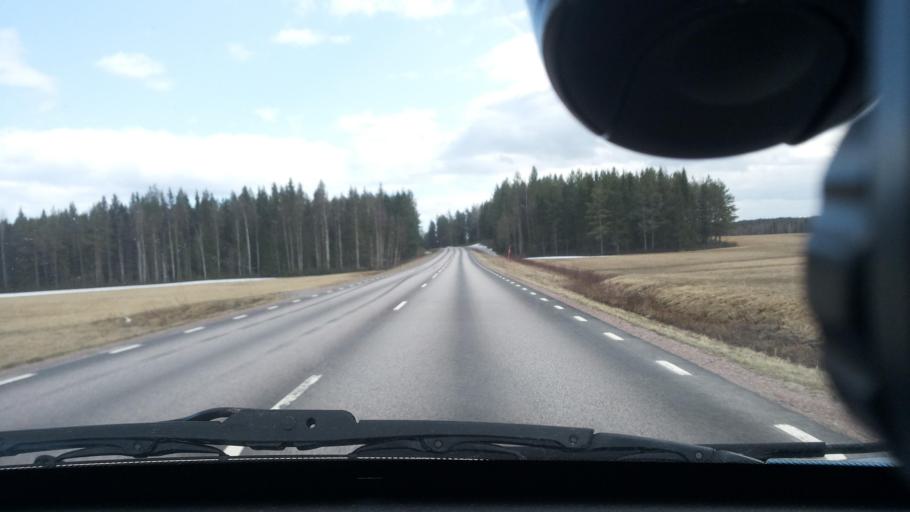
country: SE
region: Norrbotten
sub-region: Lulea Kommun
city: Sodra Sunderbyn
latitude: 65.6100
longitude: 21.9581
